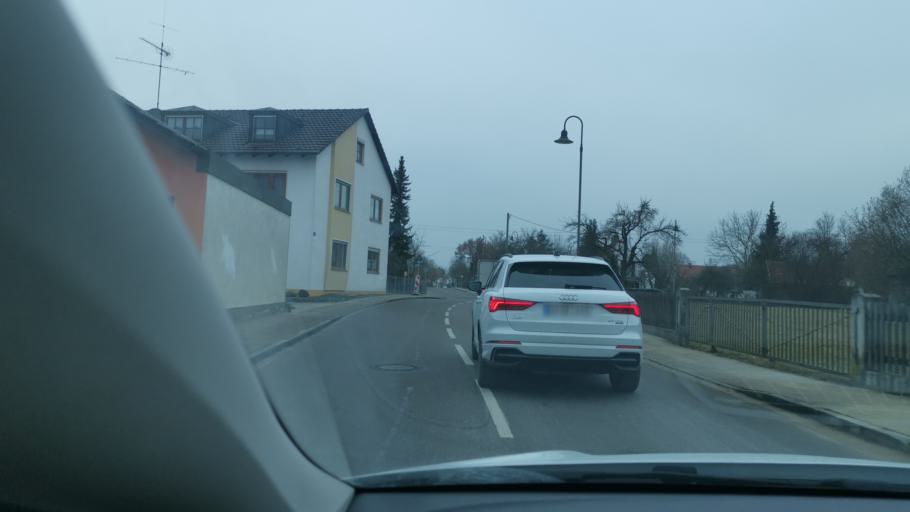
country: DE
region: Bavaria
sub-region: Swabia
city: Thierhaupten
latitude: 48.5666
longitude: 10.9079
